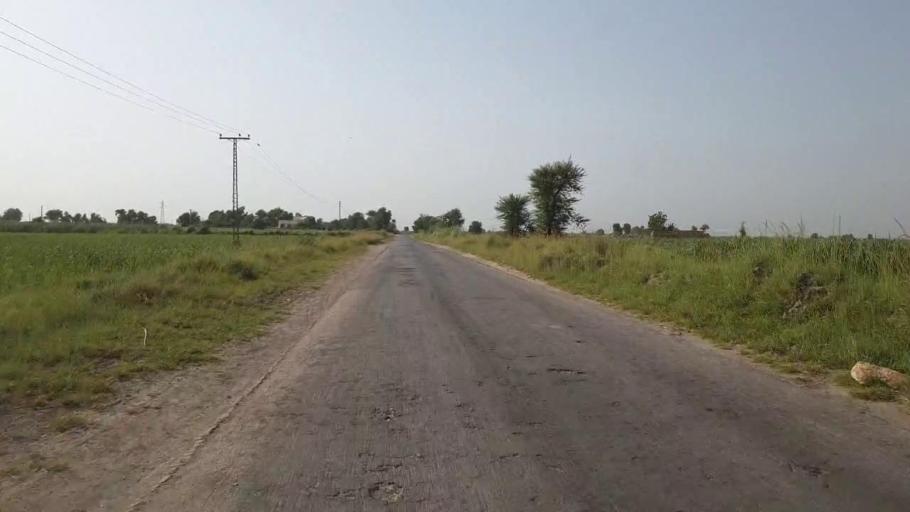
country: PK
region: Sindh
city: Khadro
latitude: 26.3585
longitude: 68.9201
